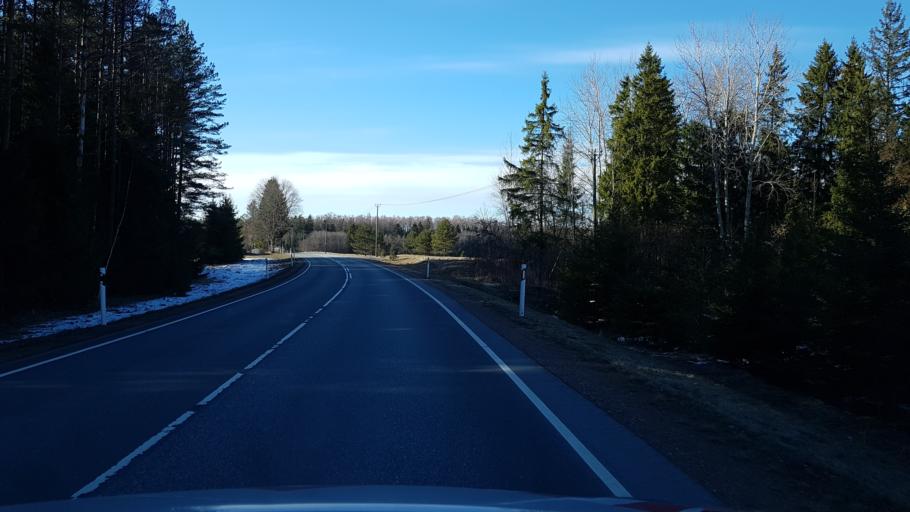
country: EE
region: Laeaene-Virumaa
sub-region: Tapa vald
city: Tapa
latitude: 59.4131
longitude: 25.9999
